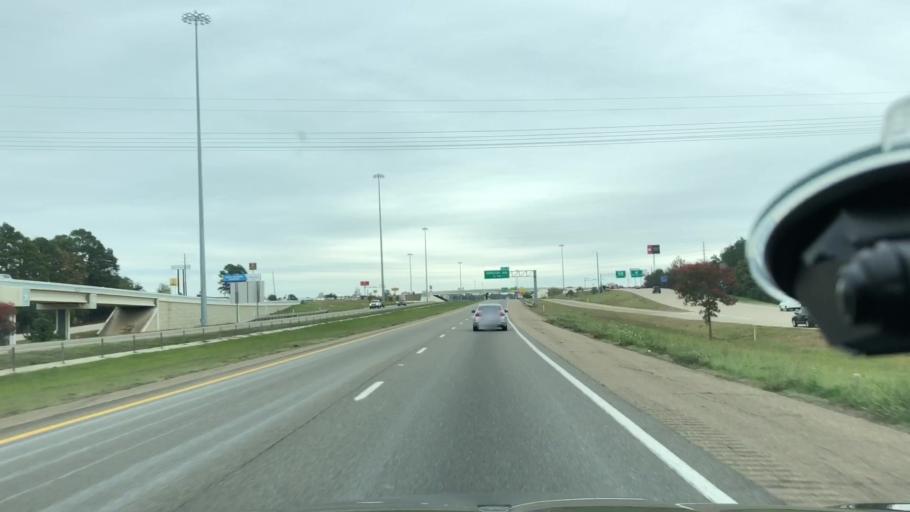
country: US
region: Arkansas
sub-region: Miller County
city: Texarkana
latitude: 33.4701
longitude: -94.0493
